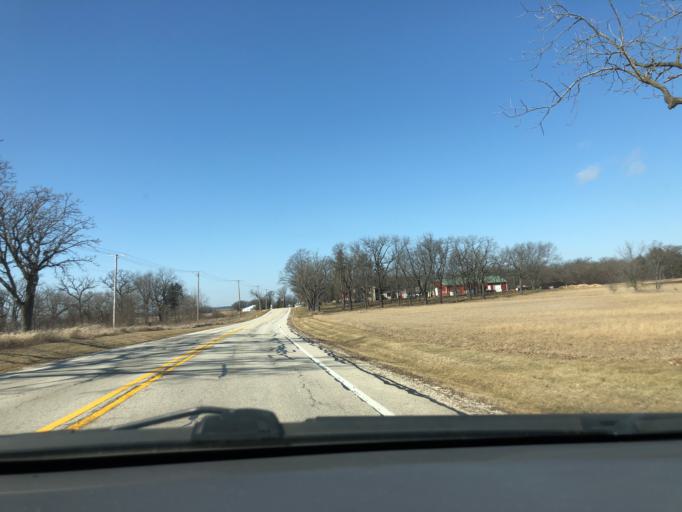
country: US
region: Illinois
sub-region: Kane County
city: Hampshire
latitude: 42.1281
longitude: -88.5201
